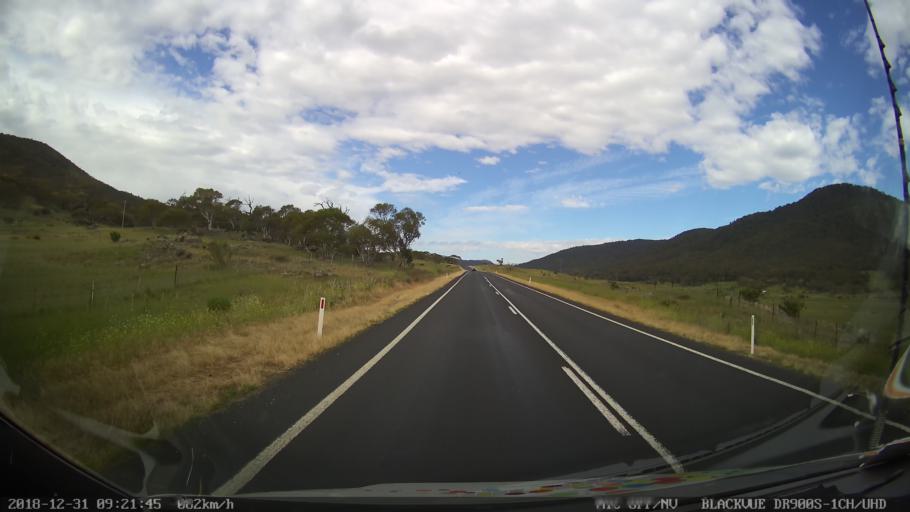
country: AU
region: New South Wales
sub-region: Snowy River
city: Jindabyne
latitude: -36.4309
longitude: 148.5572
